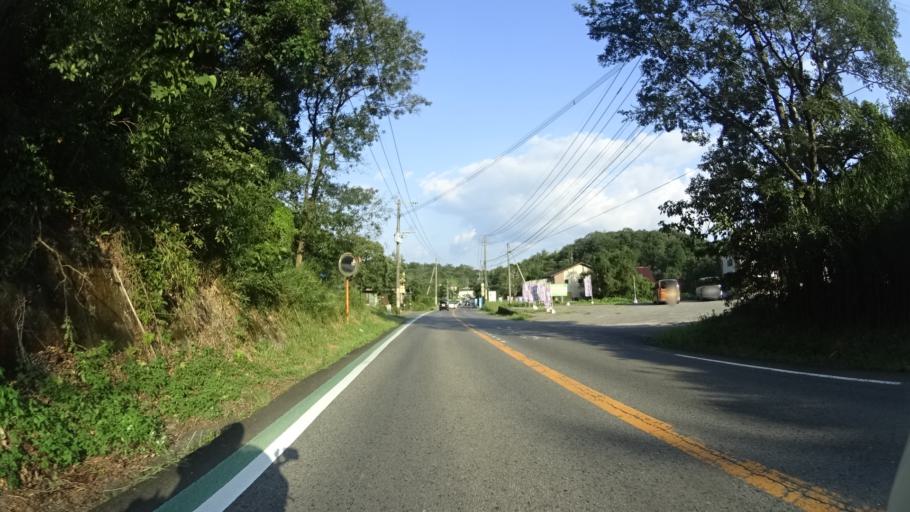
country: JP
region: Oita
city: Bungo-Takada-shi
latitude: 33.4454
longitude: 131.3414
